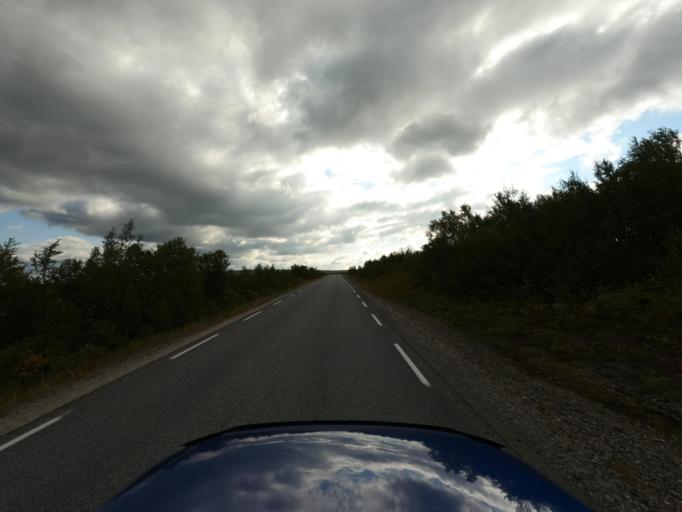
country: NO
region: Finnmark Fylke
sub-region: Porsanger
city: Lakselv
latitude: 69.3709
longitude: 24.2772
